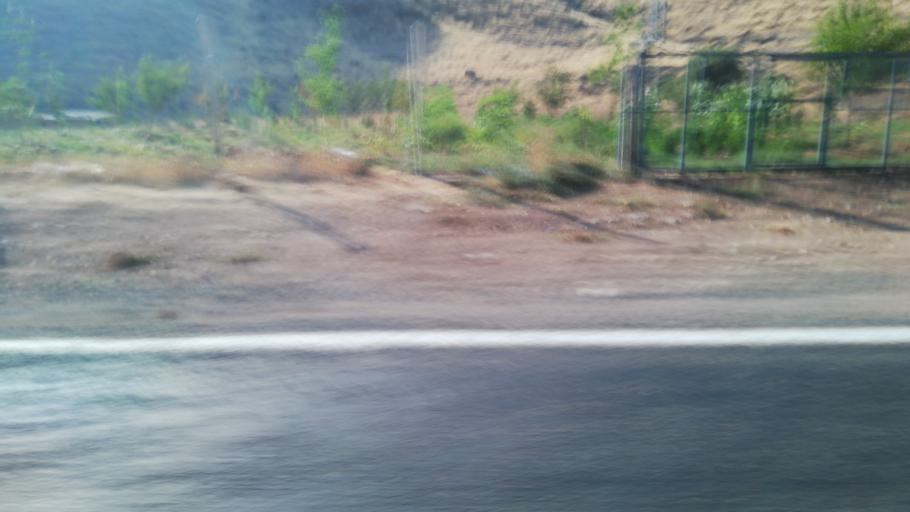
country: TR
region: Mardin
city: Sivrice
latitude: 37.2347
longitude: 41.3333
